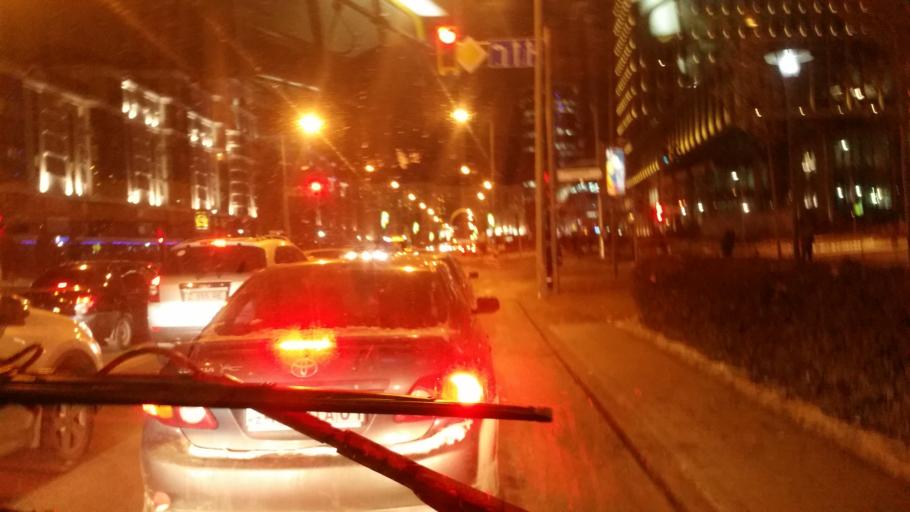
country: KZ
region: Astana Qalasy
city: Astana
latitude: 51.1257
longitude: 71.4308
